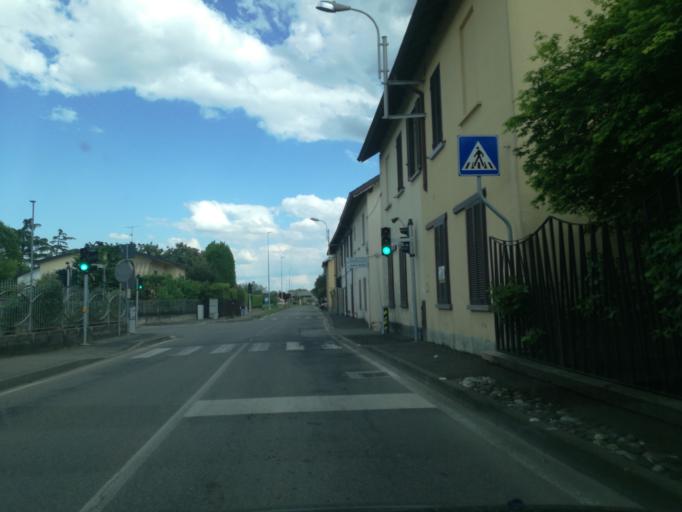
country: IT
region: Lombardy
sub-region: Provincia di Monza e Brianza
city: Ronco Briantino
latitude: 45.6657
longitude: 9.4081
